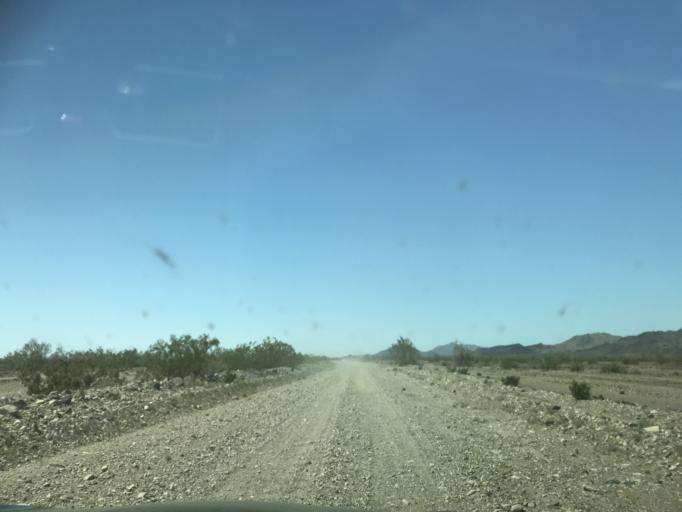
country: US
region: California
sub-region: Riverside County
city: Mesa Verde
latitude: 33.4792
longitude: -114.9344
